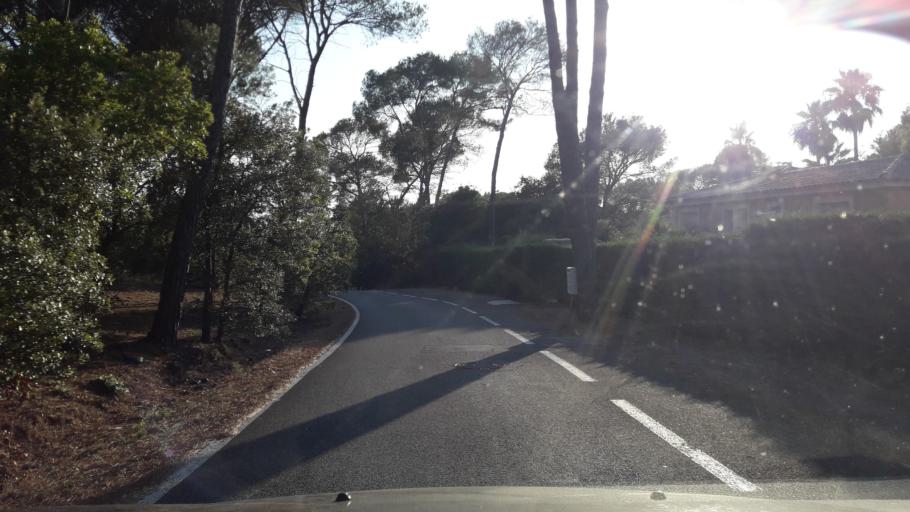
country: FR
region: Provence-Alpes-Cote d'Azur
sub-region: Departement du Var
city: Saint-Raphael
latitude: 43.4440
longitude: 6.8012
